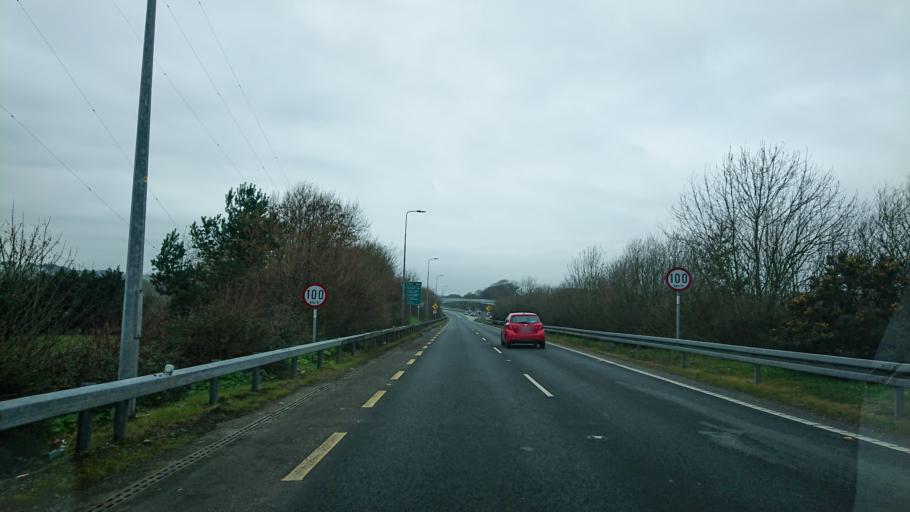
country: IE
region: Munster
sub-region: County Cork
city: Passage West
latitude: 51.8832
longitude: -8.3984
